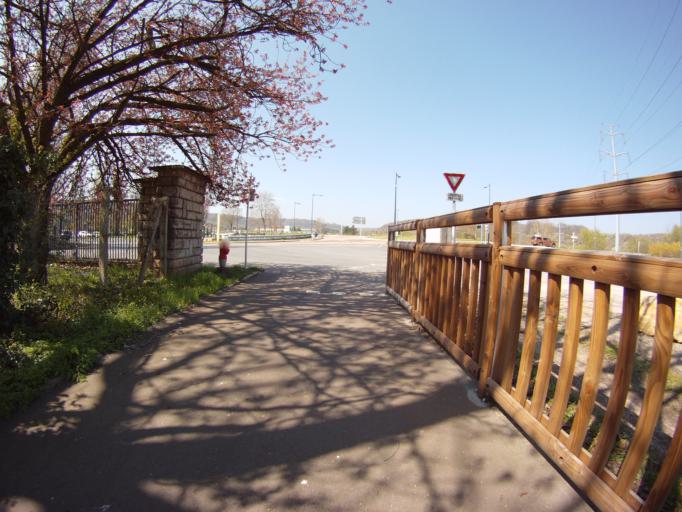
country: FR
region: Lorraine
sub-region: Departement de Meurthe-et-Moselle
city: Custines
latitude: 48.7877
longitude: 6.1392
